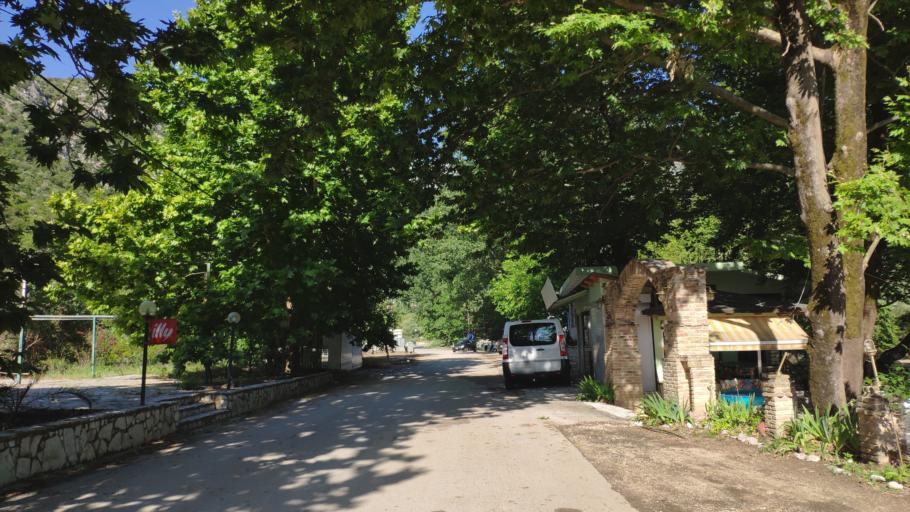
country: GR
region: Epirus
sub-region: Nomos Prevezis
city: Kanalaki
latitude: 39.3275
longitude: 20.6158
